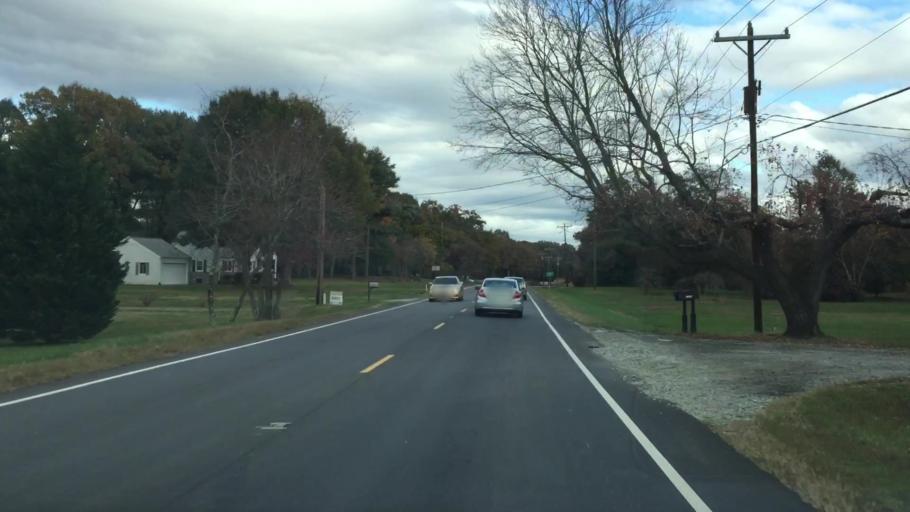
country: US
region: North Carolina
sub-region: Guilford County
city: Summerfield
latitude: 36.2528
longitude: -79.8965
